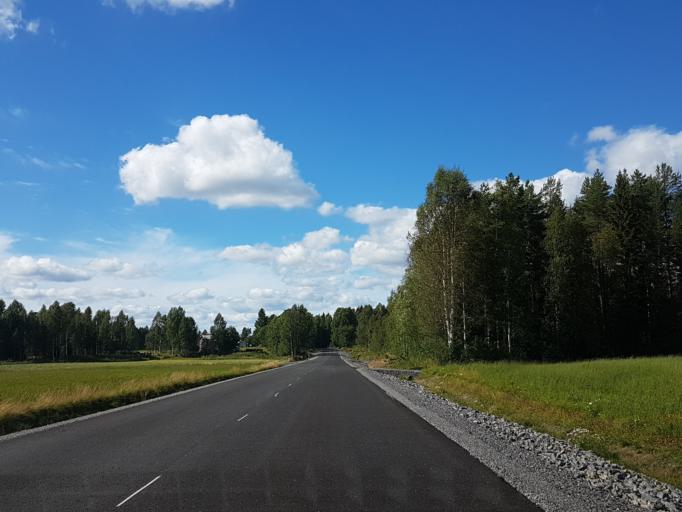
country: SE
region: Vaesterbotten
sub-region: Robertsfors Kommun
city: Robertsfors
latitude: 64.1362
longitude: 20.6294
